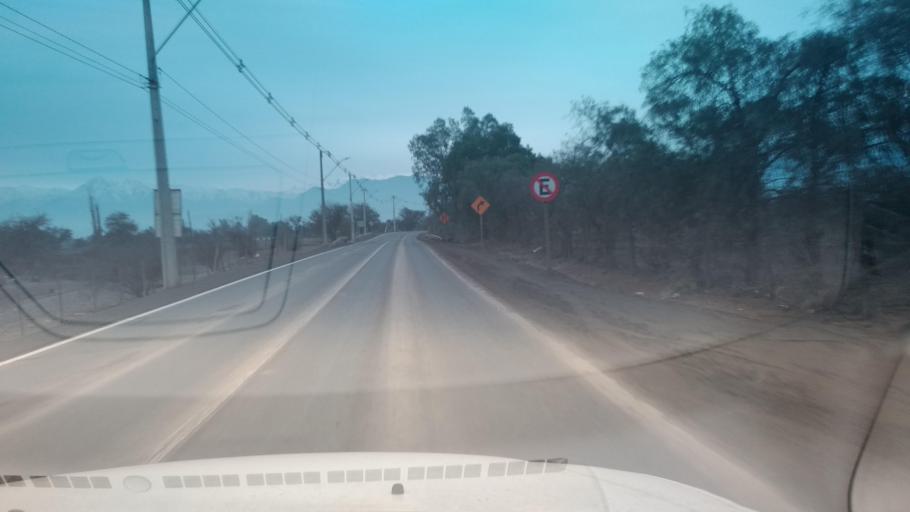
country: CL
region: Santiago Metropolitan
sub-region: Provincia de Chacabuco
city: Chicureo Abajo
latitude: -33.0925
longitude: -70.7408
